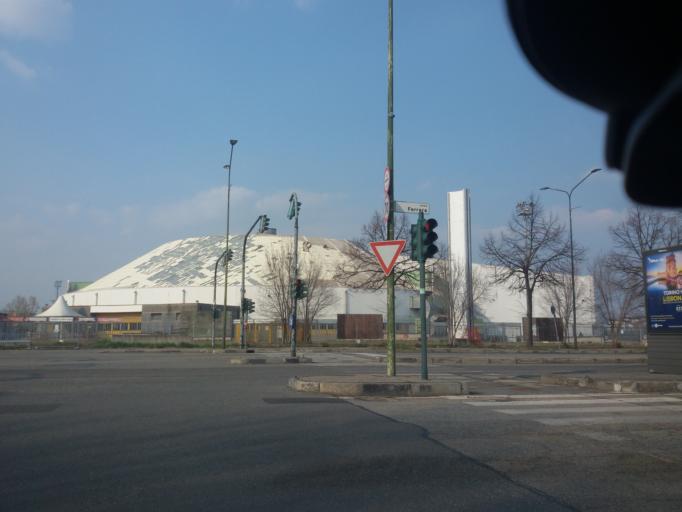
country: IT
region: Piedmont
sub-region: Provincia di Torino
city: Venaria Reale
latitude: 45.1068
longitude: 7.6333
